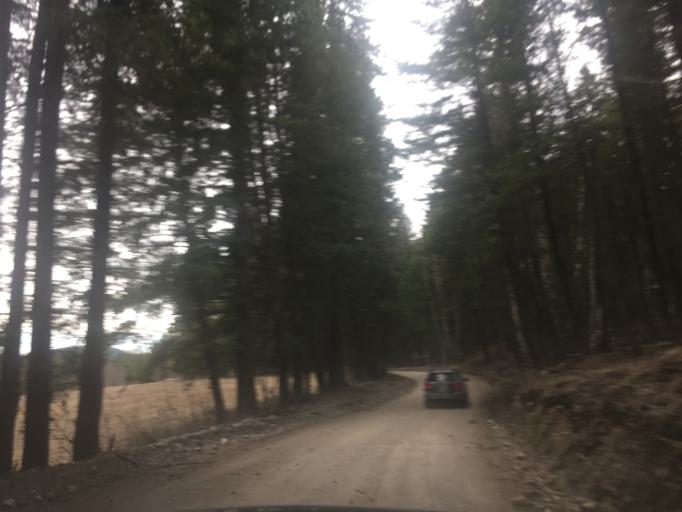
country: CA
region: British Columbia
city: Chase
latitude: 51.4006
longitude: -120.1249
